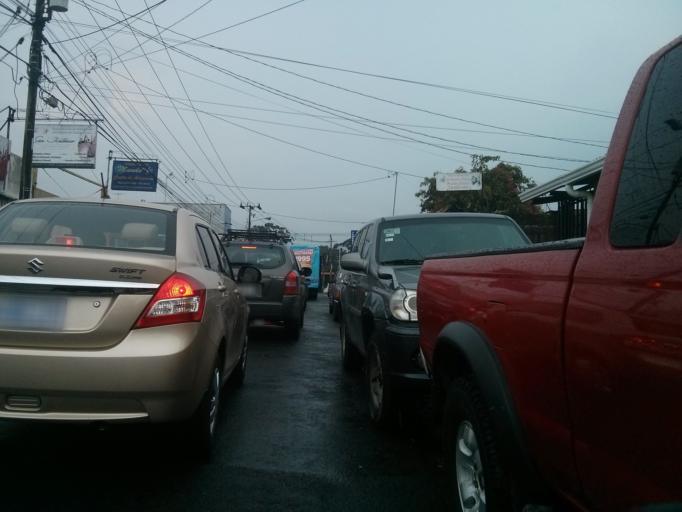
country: CR
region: San Jose
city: Curridabat
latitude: 9.9003
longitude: -84.0592
